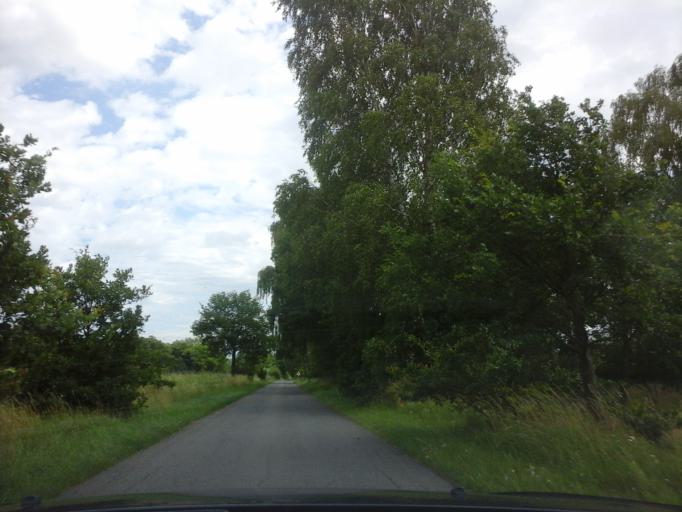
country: PL
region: West Pomeranian Voivodeship
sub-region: Powiat choszczenski
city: Recz
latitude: 53.2922
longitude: 15.5334
